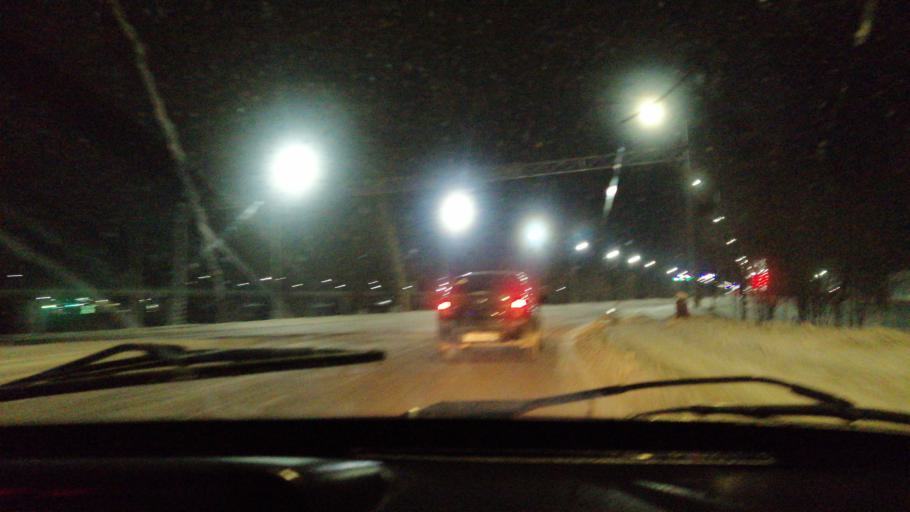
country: KZ
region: Aqtoebe
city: Aqtobe
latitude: 50.2969
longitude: 57.1851
